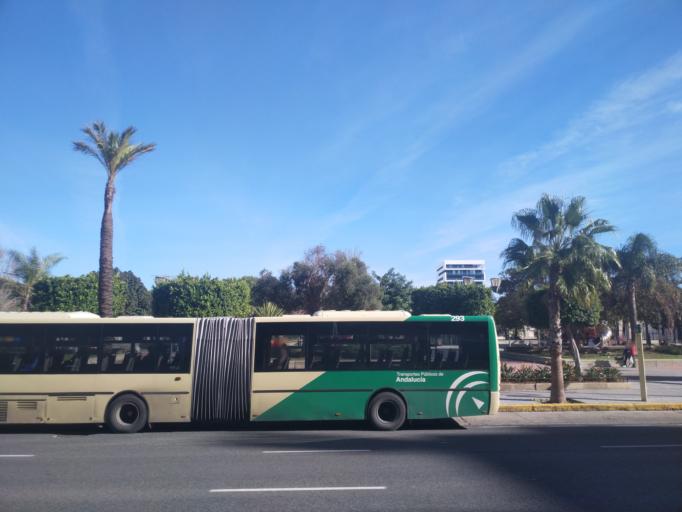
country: ES
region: Andalusia
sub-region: Provincia de Cadiz
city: Cadiz
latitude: 36.5005
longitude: -6.2735
